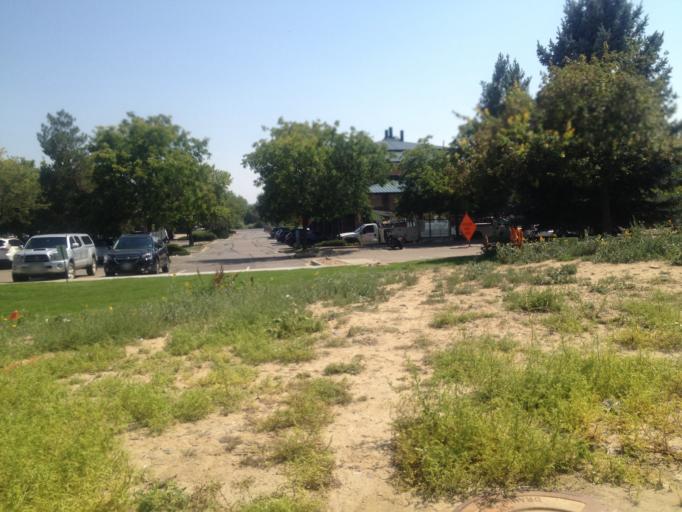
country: US
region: Colorado
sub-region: Boulder County
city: Louisville
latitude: 39.9885
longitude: -105.1294
